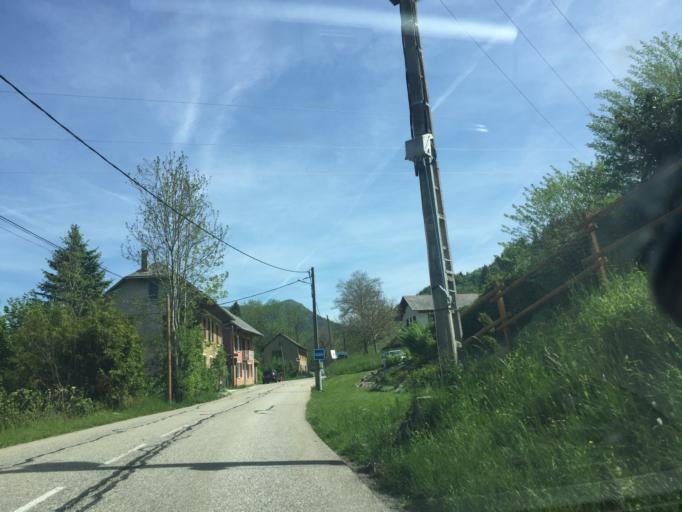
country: FR
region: Rhone-Alpes
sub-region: Departement de l'Isere
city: Barraux
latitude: 45.4472
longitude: 5.8803
